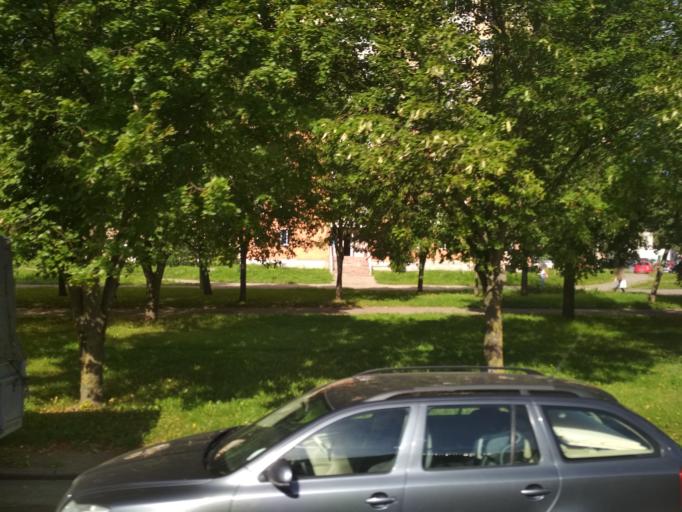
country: BY
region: Minsk
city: Minsk
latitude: 53.8839
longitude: 27.5509
